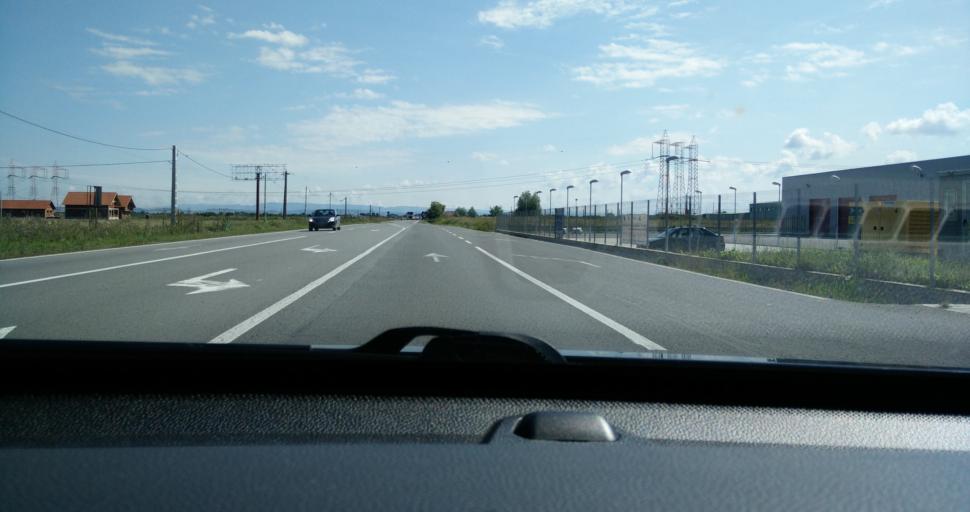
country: RO
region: Bihor
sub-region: Comuna Osorheiu
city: Osorheiu
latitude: 47.0500
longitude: 22.0511
